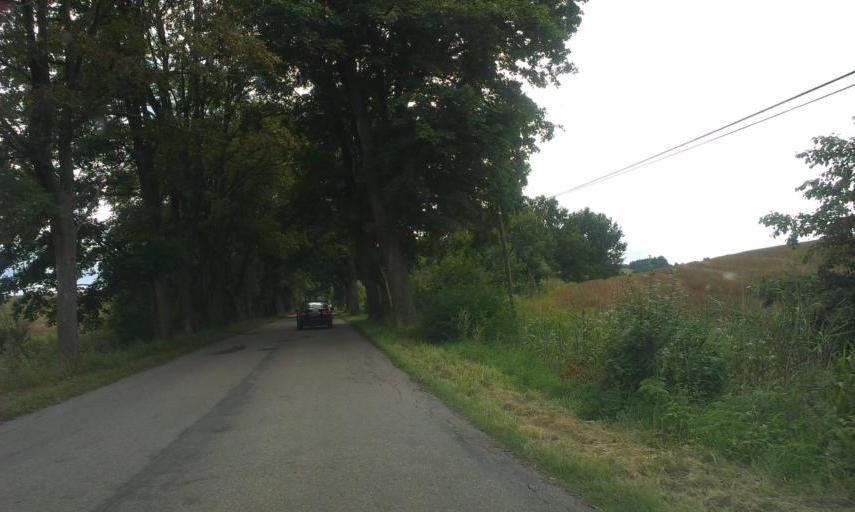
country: PL
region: West Pomeranian Voivodeship
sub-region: Powiat szczecinecki
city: Barwice
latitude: 53.7115
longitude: 16.3540
